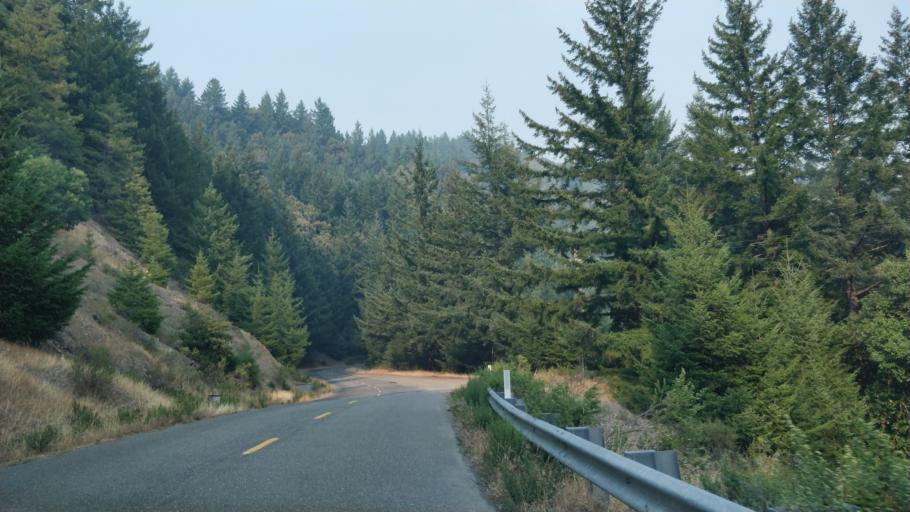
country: US
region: California
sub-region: Humboldt County
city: Rio Dell
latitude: 40.2763
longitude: -124.0781
